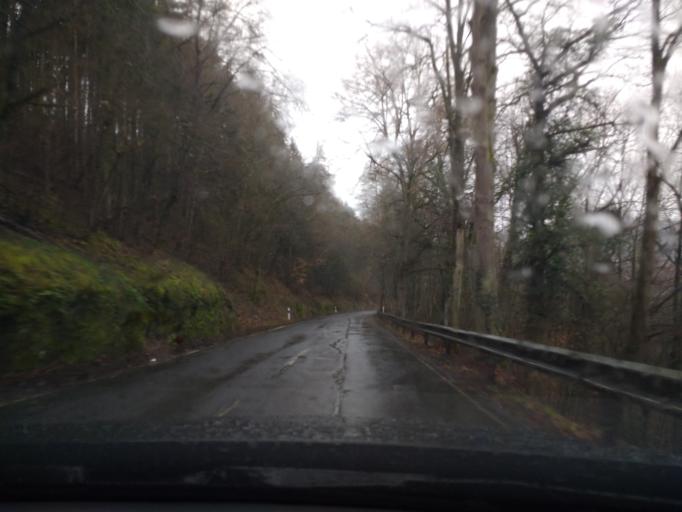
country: DE
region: Rheinland-Pfalz
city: Starkenburg
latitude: 49.9728
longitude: 7.1376
